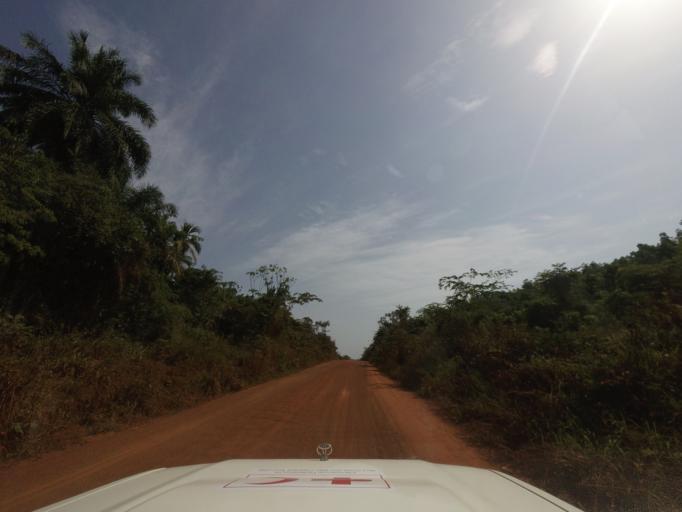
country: LR
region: Bong
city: Gbarnga
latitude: 7.0539
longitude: -9.4676
